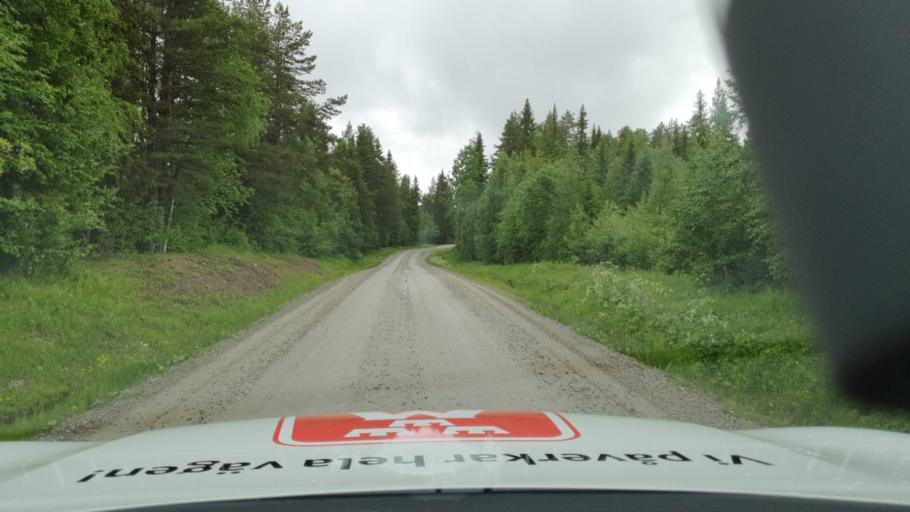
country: SE
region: Vaesterbotten
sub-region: Dorotea Kommun
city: Dorotea
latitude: 64.0346
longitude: 16.7599
